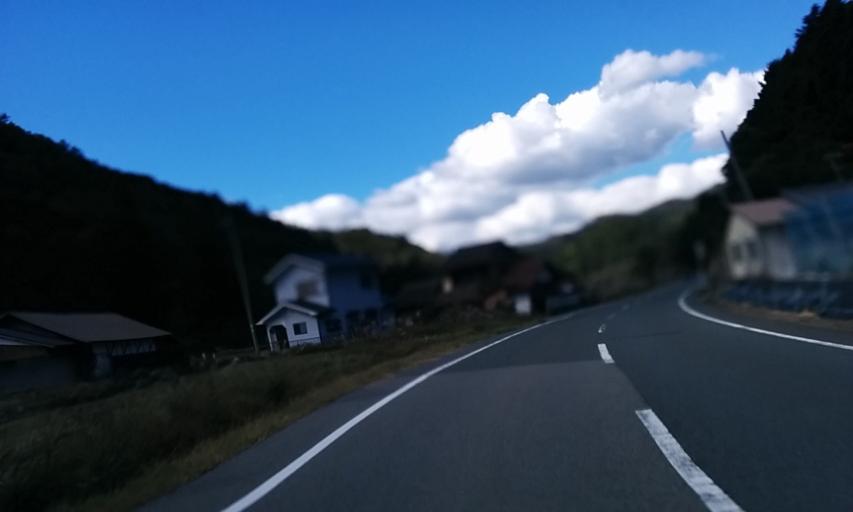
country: JP
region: Kyoto
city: Kameoka
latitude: 35.2055
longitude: 135.5776
